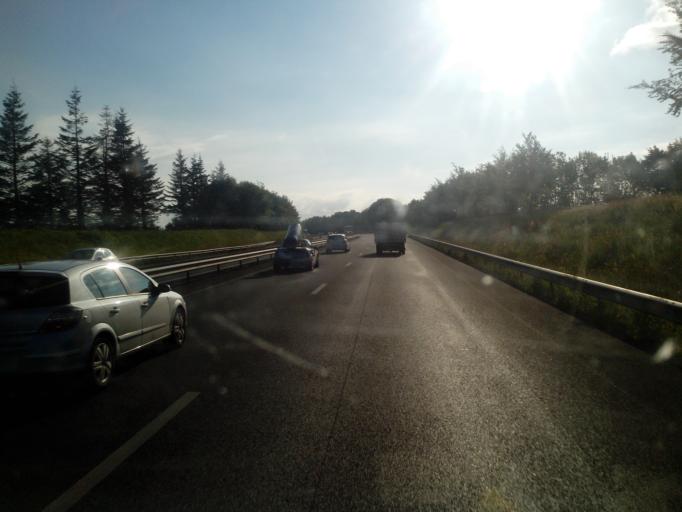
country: FR
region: Lower Normandy
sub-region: Departement du Calvados
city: Grainville-sur-Odon
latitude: 49.1436
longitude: -0.5303
